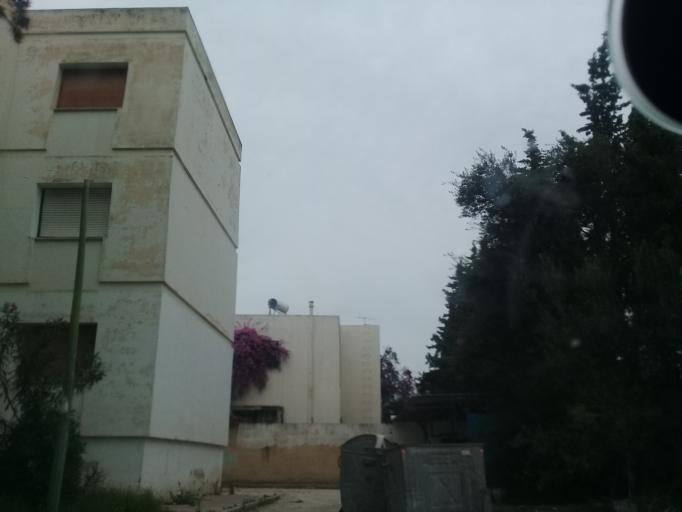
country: TN
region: Tunis
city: Tunis
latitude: 36.8391
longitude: 10.1619
